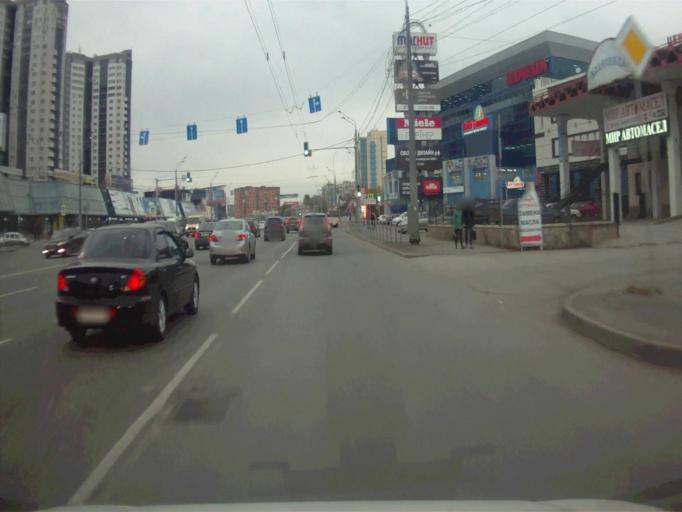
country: RU
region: Chelyabinsk
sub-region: Gorod Chelyabinsk
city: Chelyabinsk
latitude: 55.1697
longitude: 61.3739
